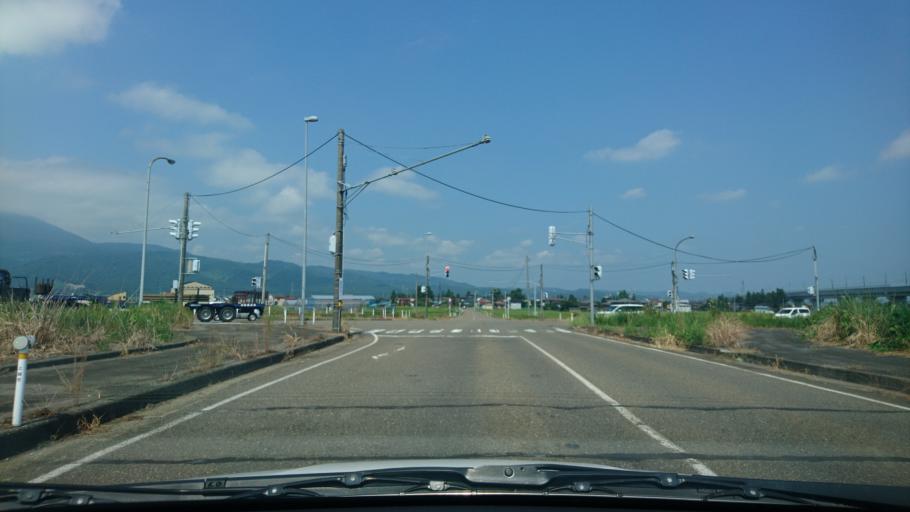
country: JP
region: Niigata
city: Arai
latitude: 37.0651
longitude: 138.2635
